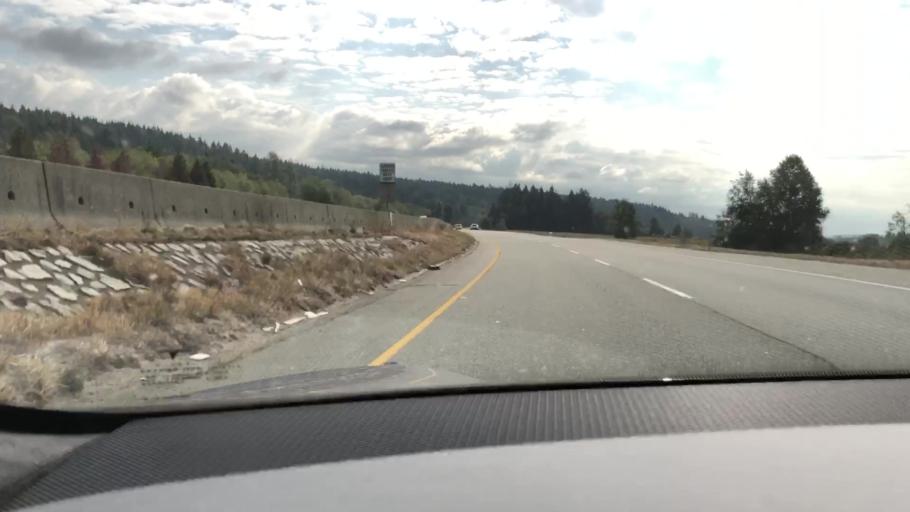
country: CA
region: British Columbia
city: Delta
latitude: 49.1152
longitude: -122.9208
